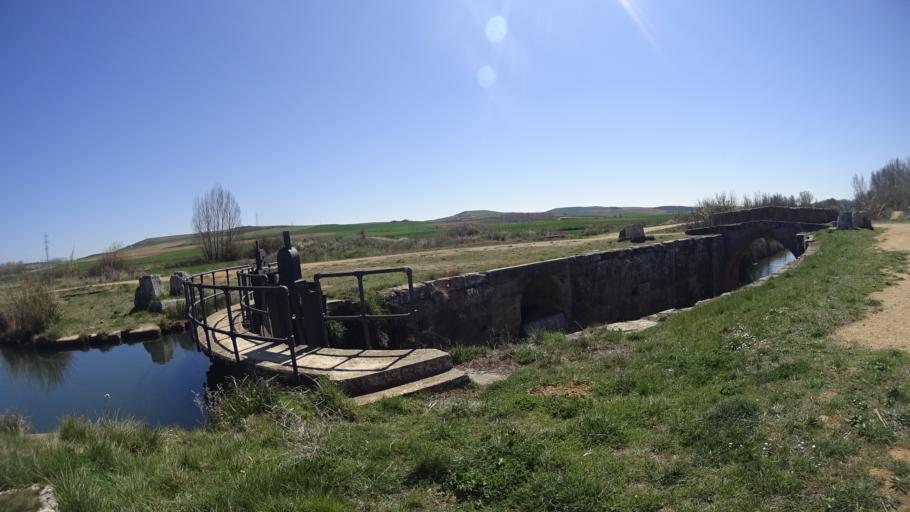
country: ES
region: Castille and Leon
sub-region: Provincia de Palencia
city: Herrera de Pisuerga
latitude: 42.6055
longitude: -4.3148
